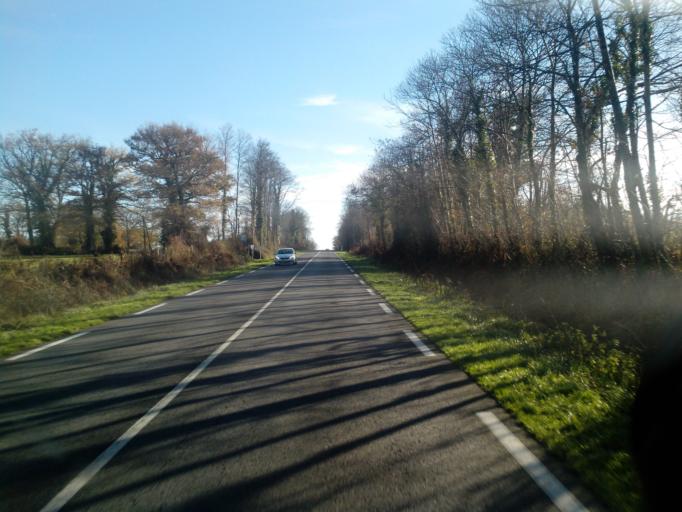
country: FR
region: Limousin
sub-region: Departement de la Haute-Vienne
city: Bussiere-Poitevine
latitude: 46.1778
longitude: 0.9424
